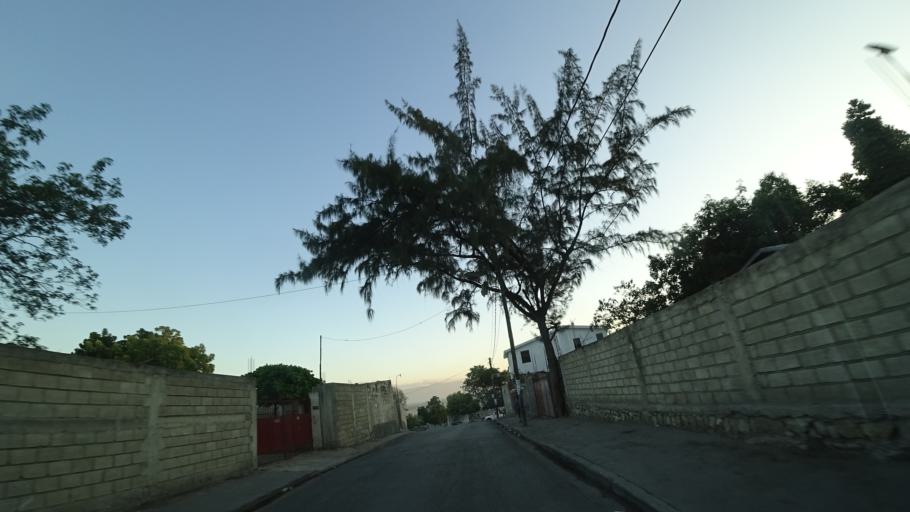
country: HT
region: Ouest
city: Delmas 73
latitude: 18.5655
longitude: -72.2986
